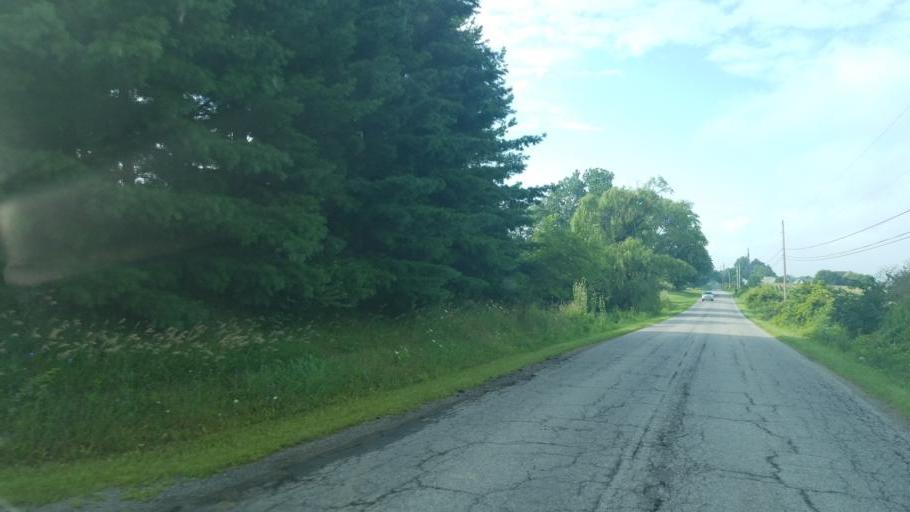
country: US
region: Ohio
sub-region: Morrow County
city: Mount Gilead
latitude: 40.5036
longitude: -82.8369
